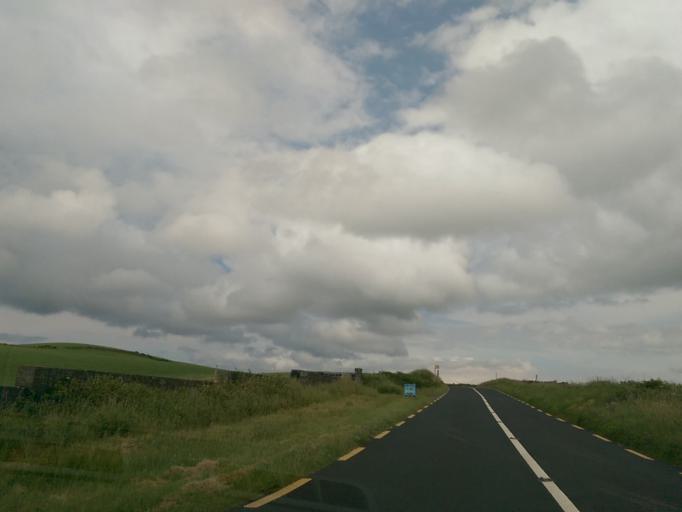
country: IE
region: Munster
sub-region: An Clar
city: Kilrush
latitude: 52.6971
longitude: -9.6293
